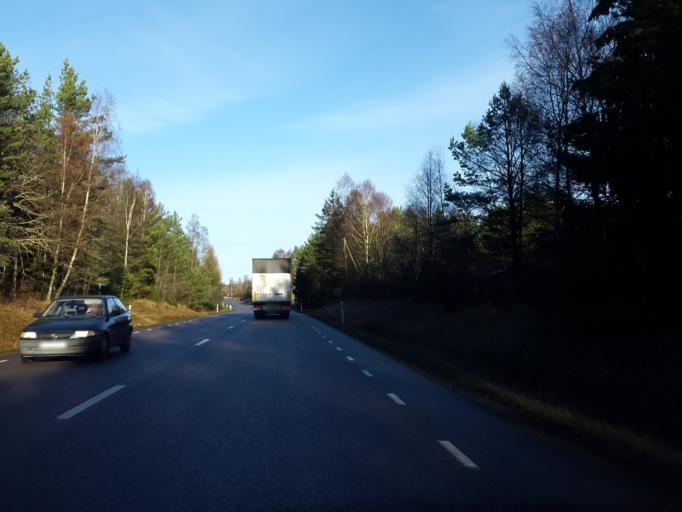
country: SE
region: Vaestra Goetaland
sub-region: Vargarda Kommun
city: Vargarda
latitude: 58.0045
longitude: 12.8141
